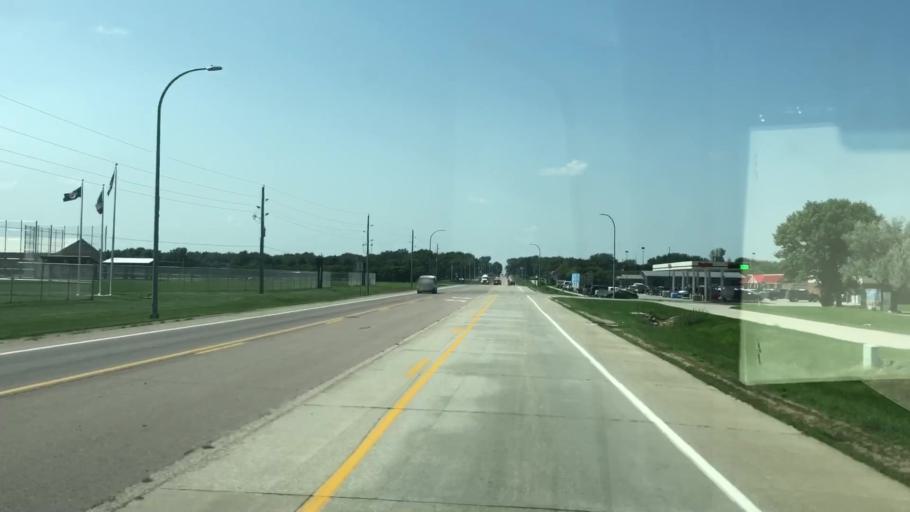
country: US
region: Iowa
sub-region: O'Brien County
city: Sheldon
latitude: 43.1861
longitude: -95.8291
